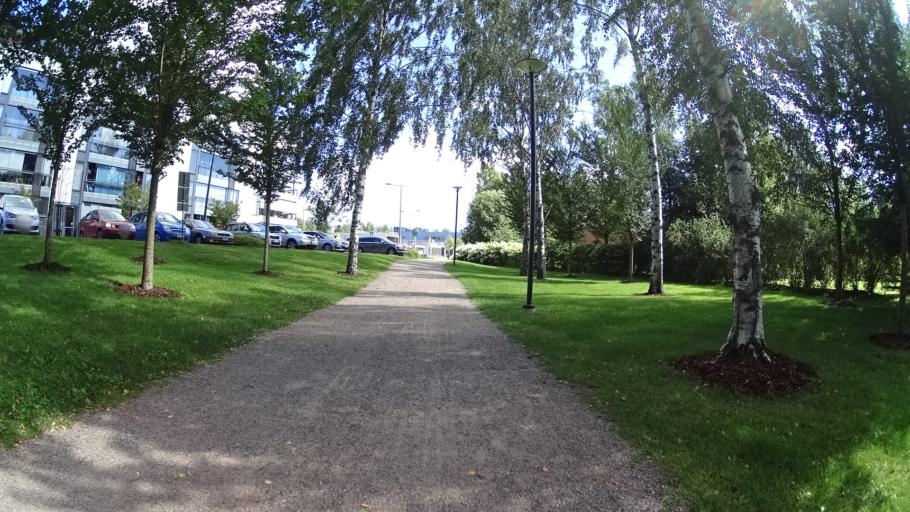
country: FI
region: Uusimaa
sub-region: Helsinki
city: Kauniainen
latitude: 60.2101
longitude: 24.7246
